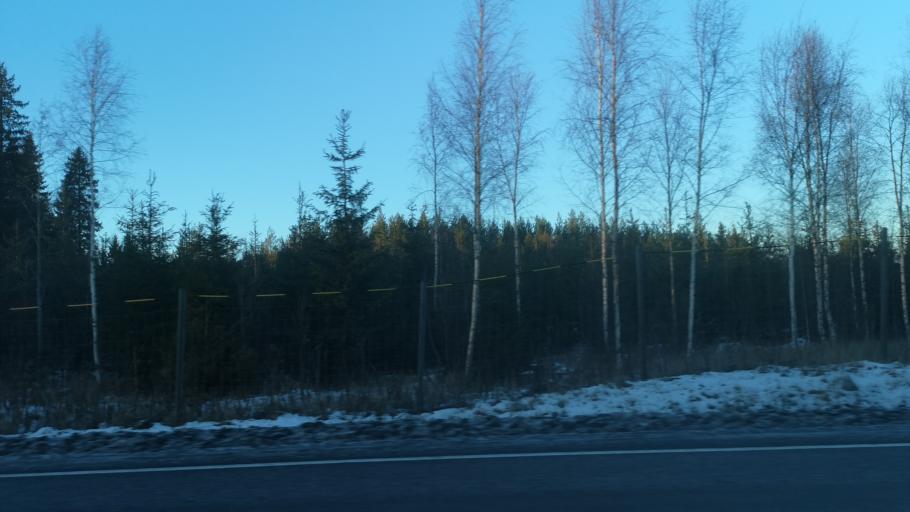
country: FI
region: Southern Savonia
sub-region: Pieksaemaeki
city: Juva
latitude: 61.8346
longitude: 27.6515
